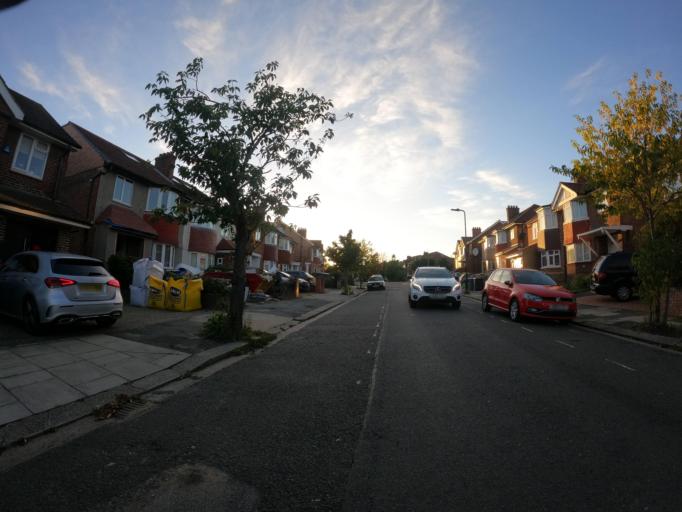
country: GB
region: England
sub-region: Greater London
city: Acton
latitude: 51.5132
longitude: -0.2542
